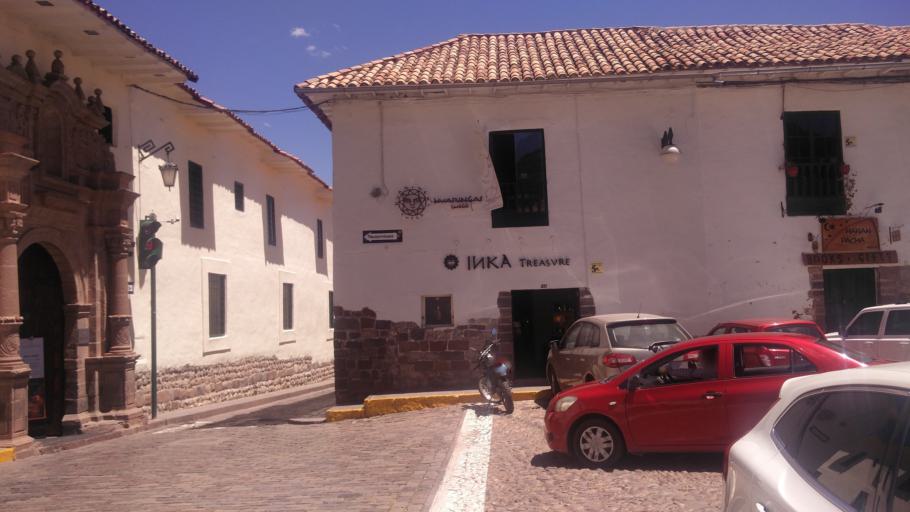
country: PE
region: Cusco
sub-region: Provincia de Cusco
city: Cusco
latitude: -13.5154
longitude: -71.9771
